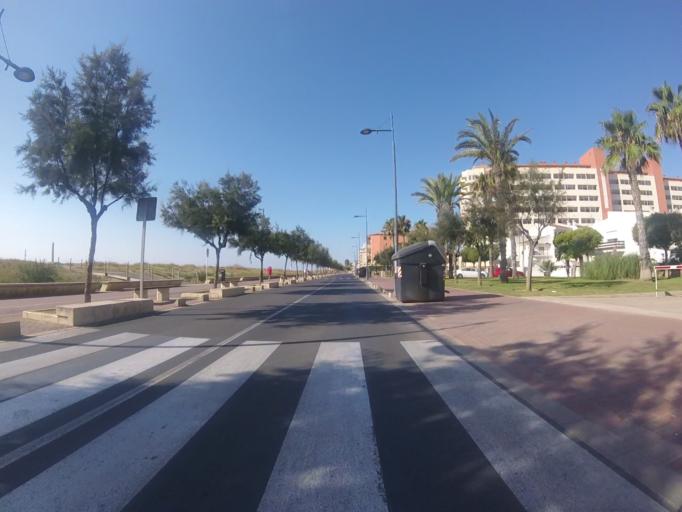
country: ES
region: Valencia
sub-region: Provincia de Castello
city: Benicarlo
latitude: 40.3902
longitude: 0.4121
